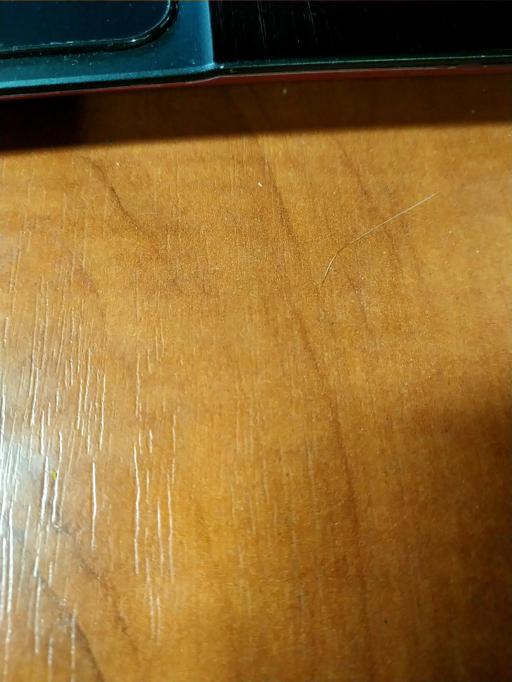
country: RU
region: Smolensk
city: Ozernyy
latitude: 55.4360
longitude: 32.7223
